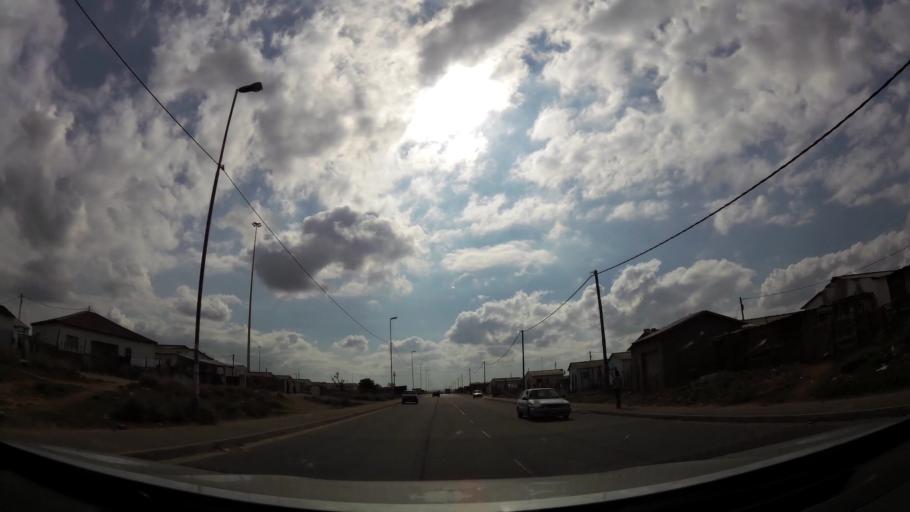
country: ZA
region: Eastern Cape
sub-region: Nelson Mandela Bay Metropolitan Municipality
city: Port Elizabeth
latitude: -33.7942
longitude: 25.5820
